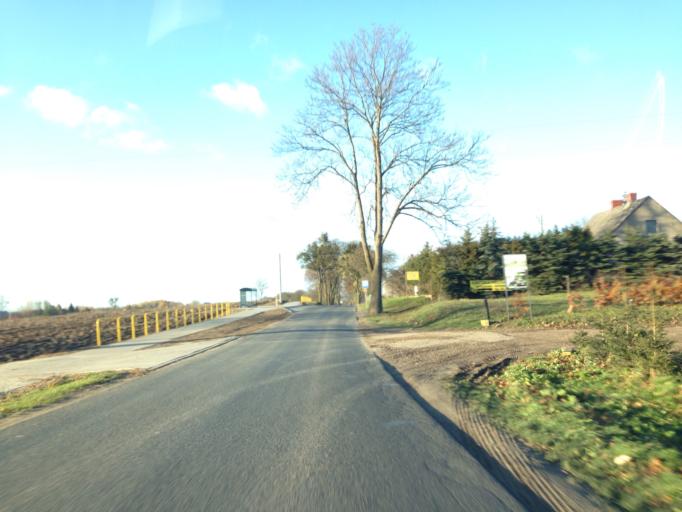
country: PL
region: Kujawsko-Pomorskie
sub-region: Powiat brodnicki
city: Brodnica
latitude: 53.3145
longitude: 19.3867
